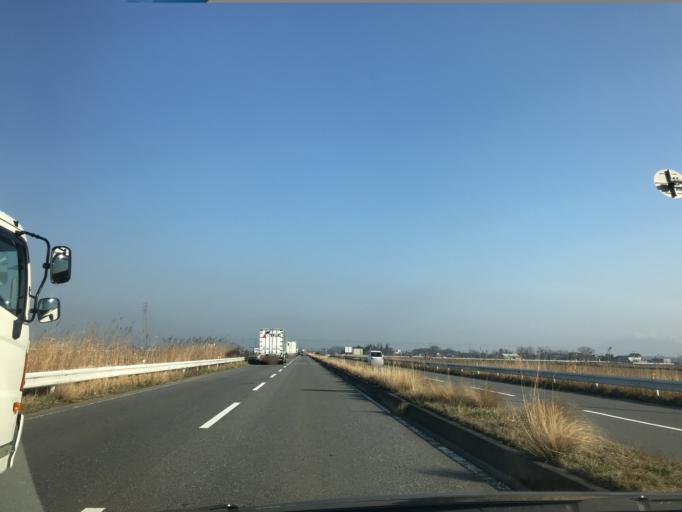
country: JP
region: Ibaraki
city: Mitsukaido
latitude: 36.0424
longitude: 139.9995
